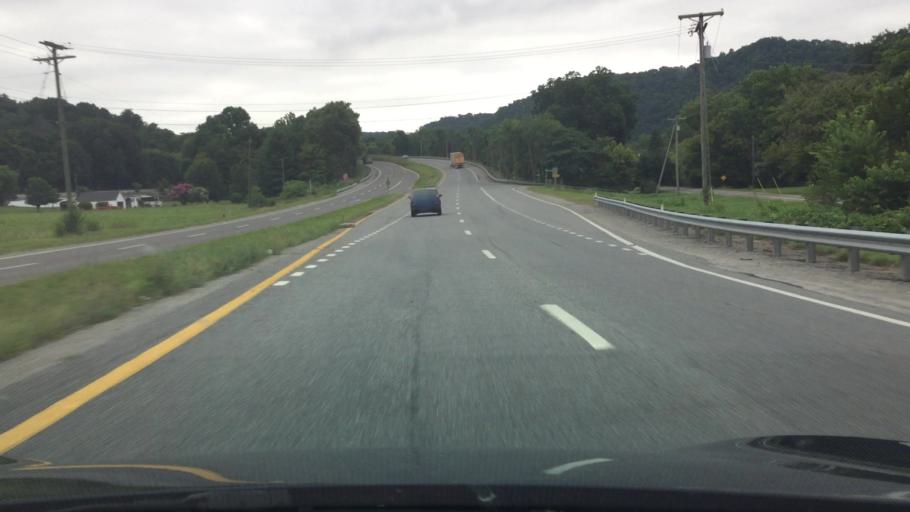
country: US
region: Virginia
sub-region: Montgomery County
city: Shawsville
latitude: 37.2213
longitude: -80.2243
